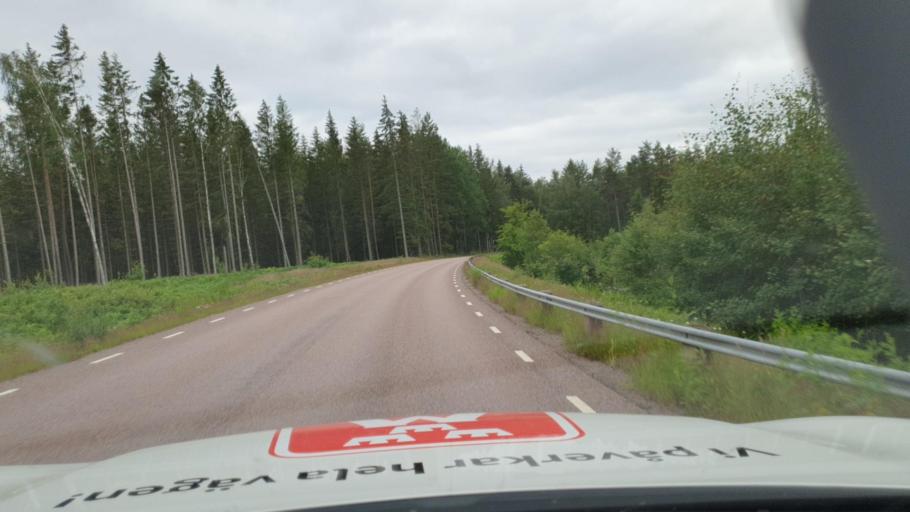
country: SE
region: Vaermland
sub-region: Forshaga Kommun
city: Forshaga
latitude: 59.4921
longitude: 13.4065
